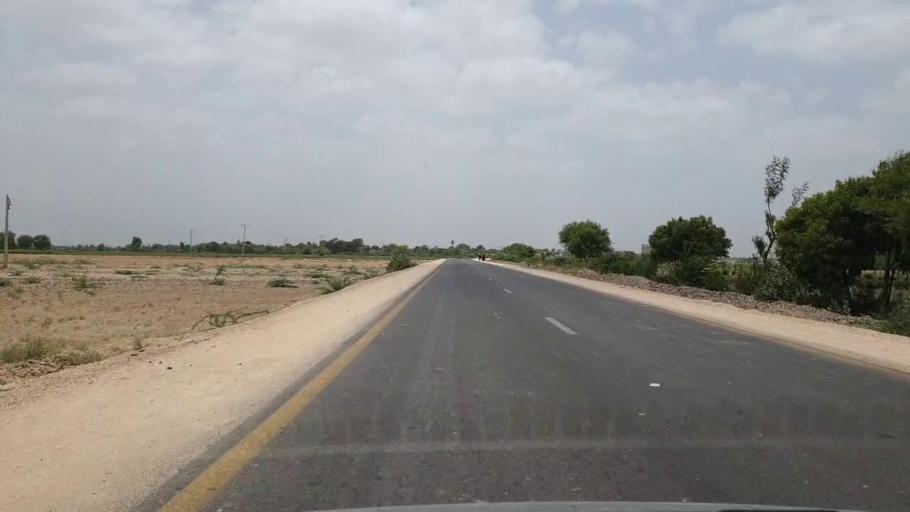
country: PK
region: Sindh
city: Naukot
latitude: 24.8432
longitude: 69.4315
